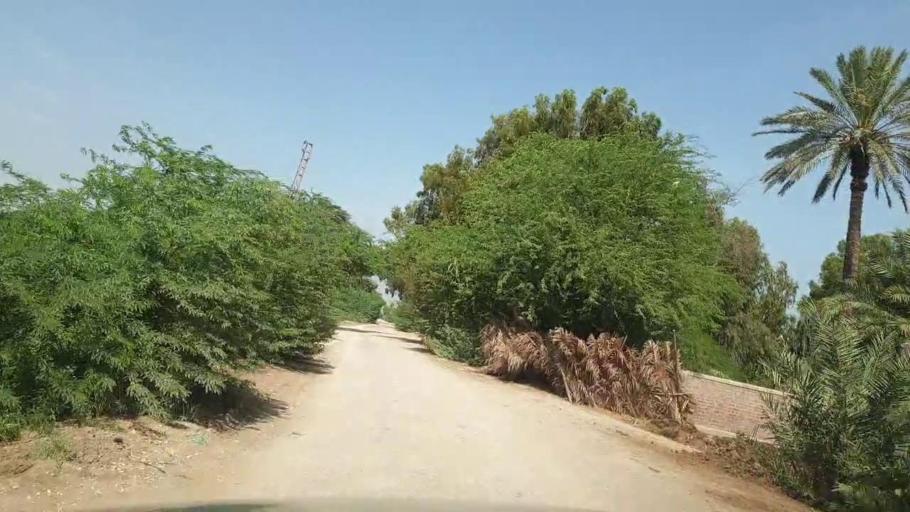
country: PK
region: Sindh
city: Rohri
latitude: 27.6885
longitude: 68.9565
